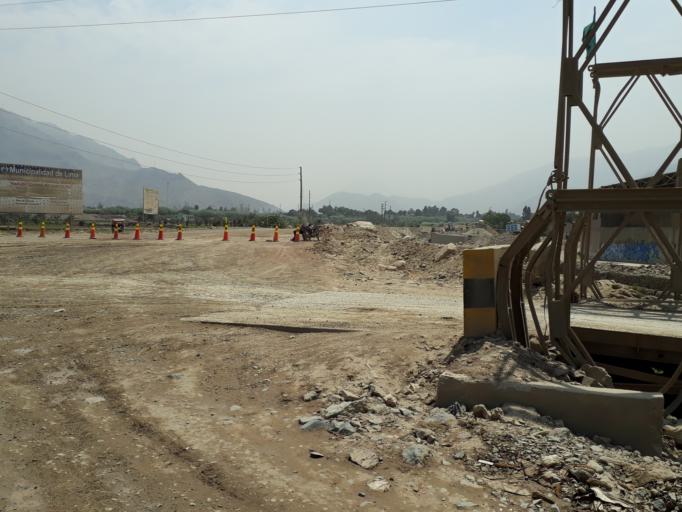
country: PE
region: Lima
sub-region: Lima
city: Santa Maria
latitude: -11.9990
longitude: -76.9162
